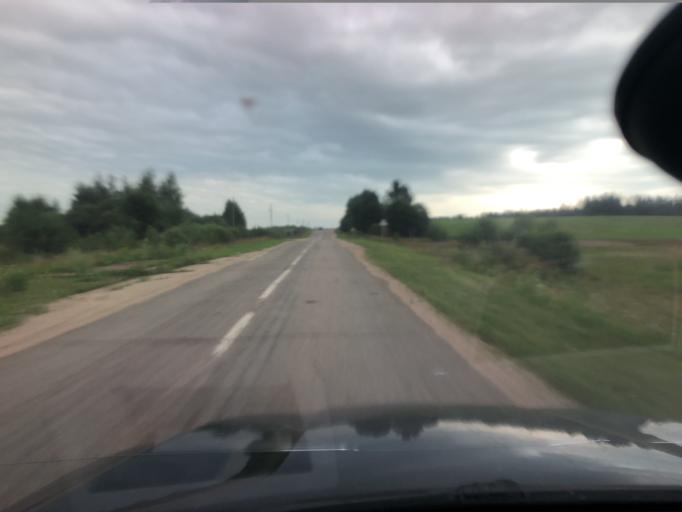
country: RU
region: Jaroslavl
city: Pereslavl'-Zalesskiy
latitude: 57.0237
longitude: 38.9385
